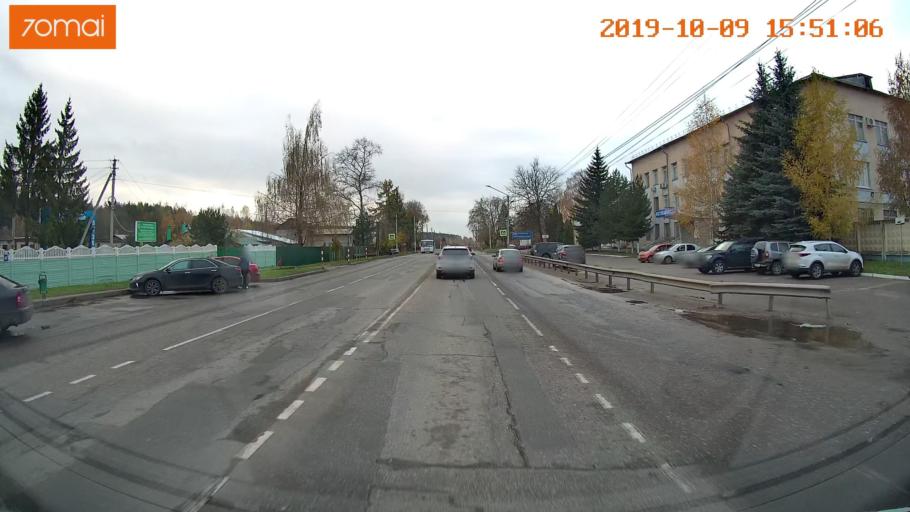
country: RU
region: Kostroma
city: Oktyabr'skiy
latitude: 57.7995
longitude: 40.9821
